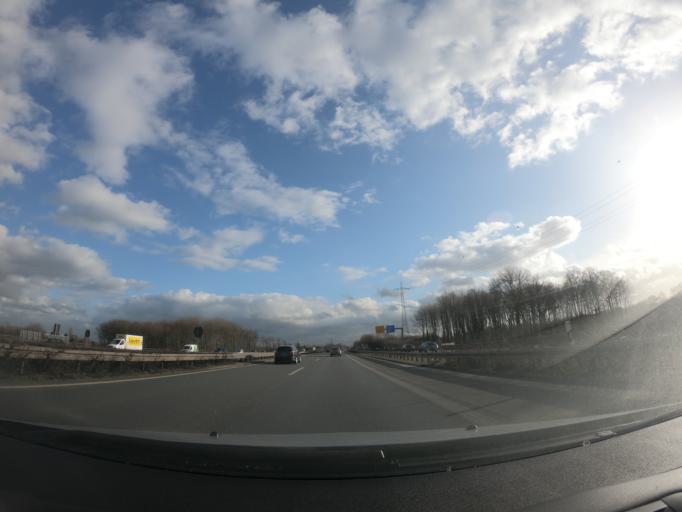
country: DE
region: North Rhine-Westphalia
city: Lunen
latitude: 51.5786
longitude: 7.4938
